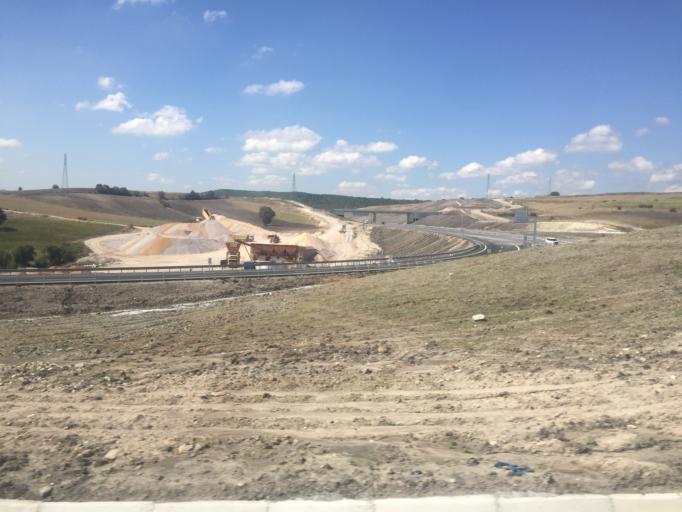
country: TR
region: Balikesir
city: Gobel
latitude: 39.9686
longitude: 28.1623
